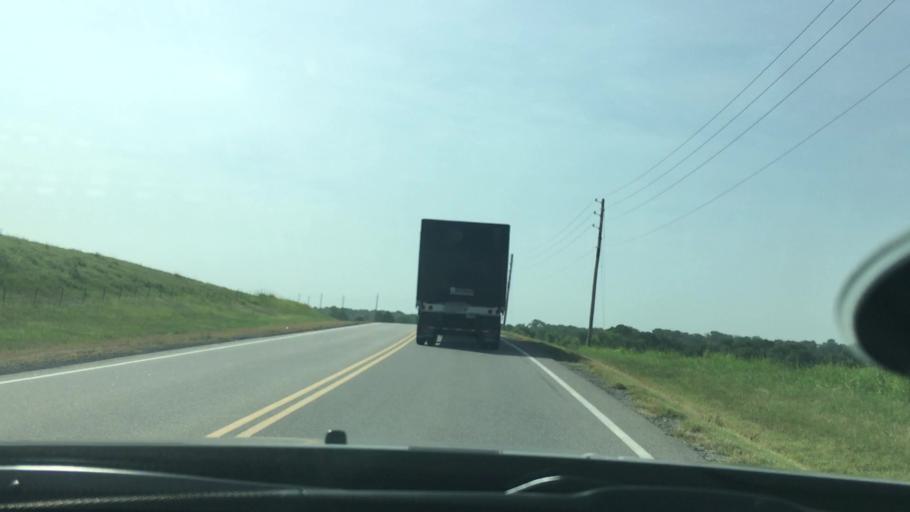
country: US
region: Oklahoma
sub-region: Atoka County
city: Atoka
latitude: 34.4041
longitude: -96.1783
